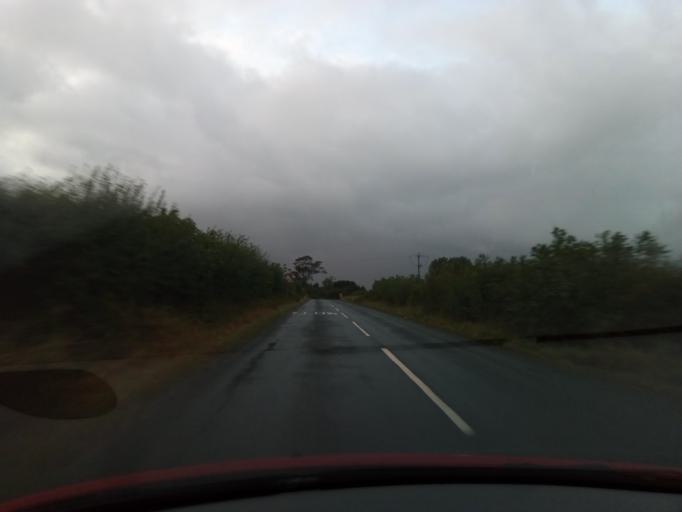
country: GB
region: England
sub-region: Darlington
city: Summerhouse
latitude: 54.6048
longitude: -1.6805
